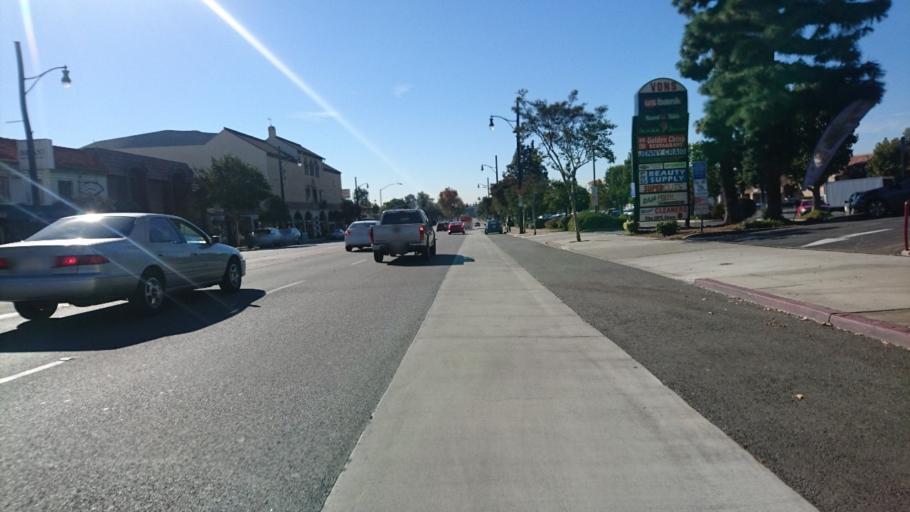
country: US
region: California
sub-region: Los Angeles County
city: South Pasadena
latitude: 34.1137
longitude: -118.1505
